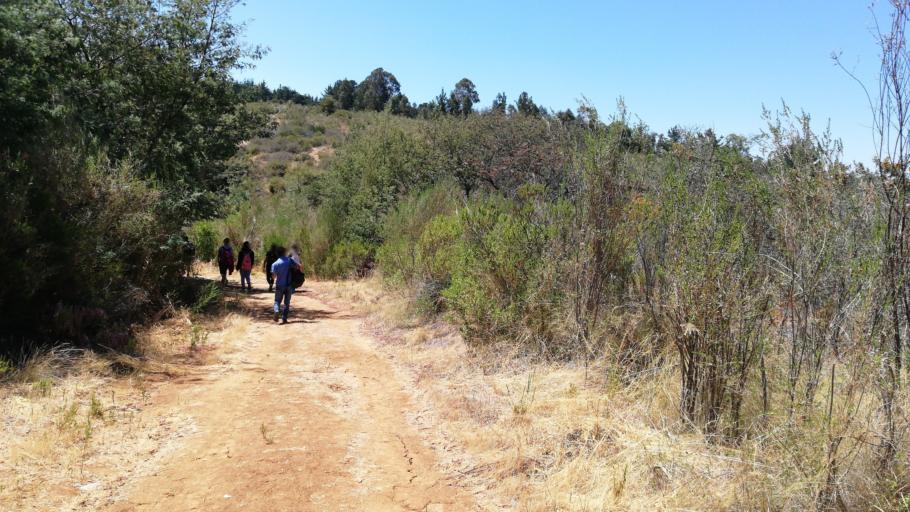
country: CL
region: Valparaiso
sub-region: Provincia de Valparaiso
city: Valparaiso
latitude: -33.0770
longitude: -71.6565
